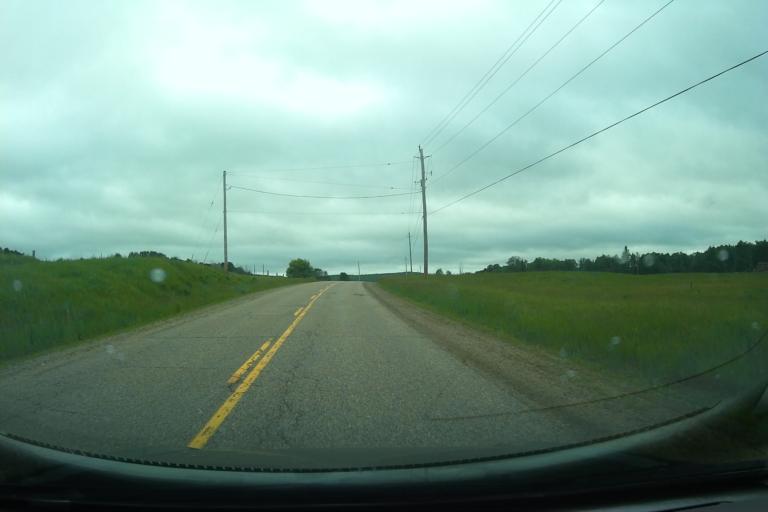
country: CA
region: Ontario
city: Pembroke
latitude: 45.4612
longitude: -77.2685
